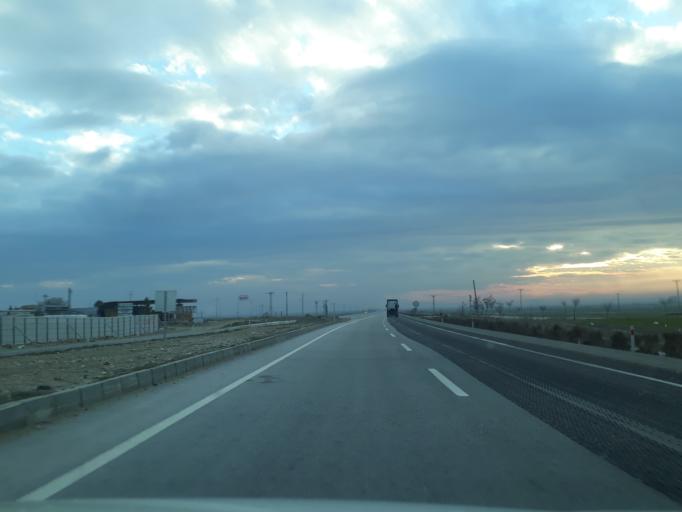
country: TR
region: Konya
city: Hotamis
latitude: 37.7106
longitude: 33.2779
